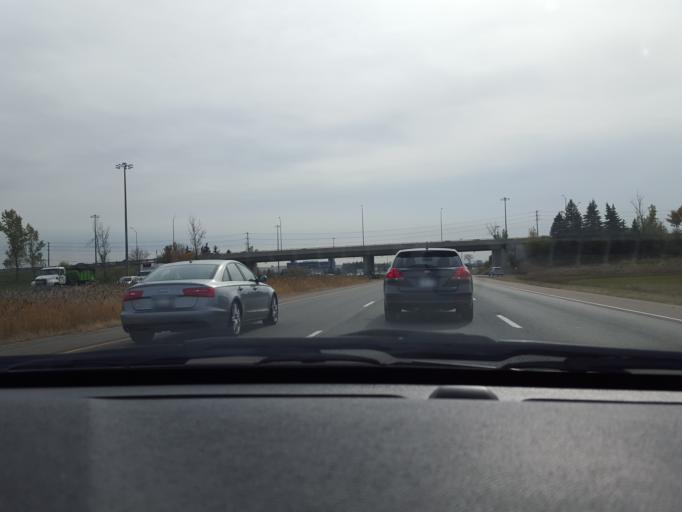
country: CA
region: Ontario
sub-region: York
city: Richmond Hill
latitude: 43.8851
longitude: -79.3805
